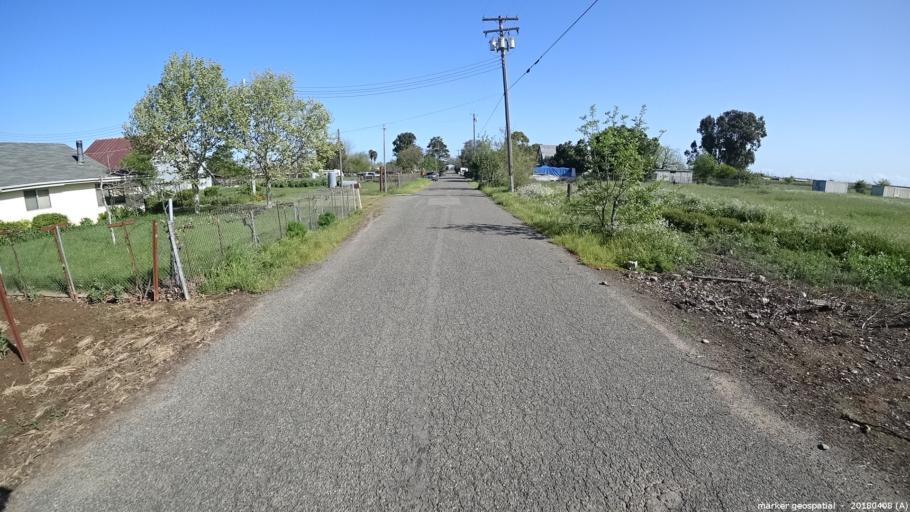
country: US
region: California
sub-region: Sacramento County
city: Elk Grove
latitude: 38.3656
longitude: -121.4037
